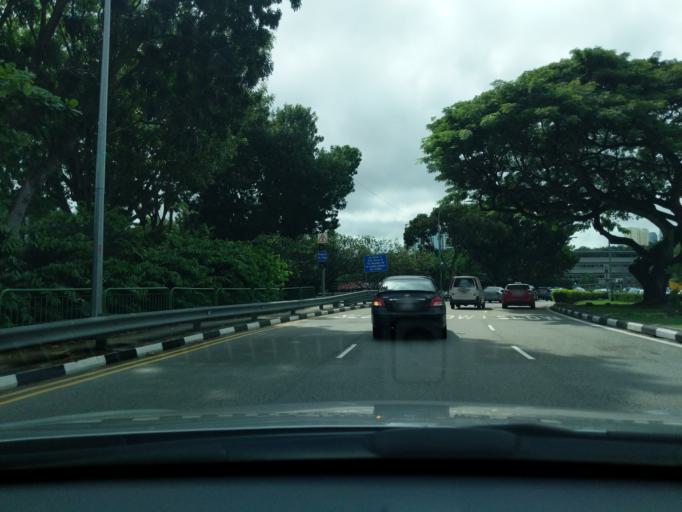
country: SG
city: Singapore
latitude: 1.3115
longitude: 103.8478
